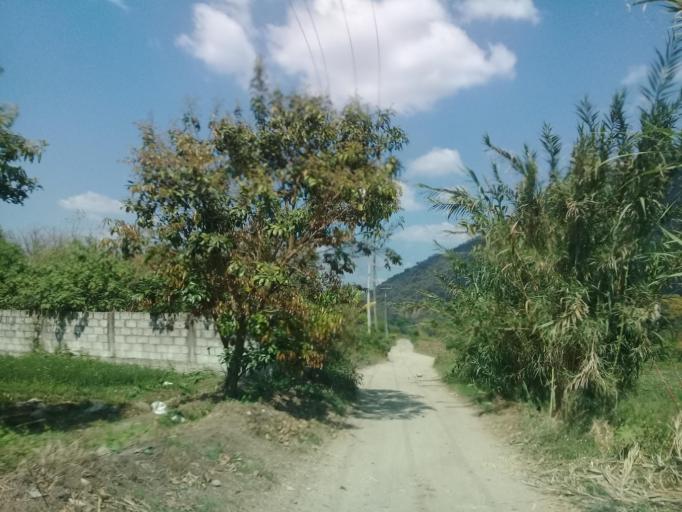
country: MX
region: Veracruz
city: Jalapilla
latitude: 18.8274
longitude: -97.0752
